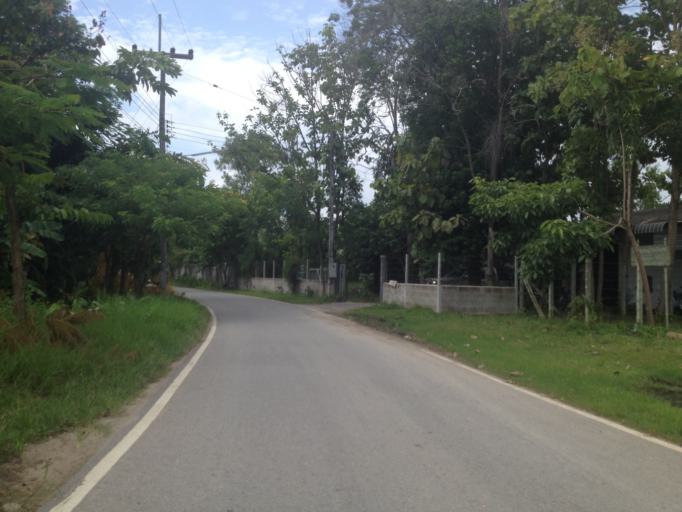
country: TH
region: Chiang Mai
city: Hang Dong
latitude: 18.6707
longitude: 98.9597
